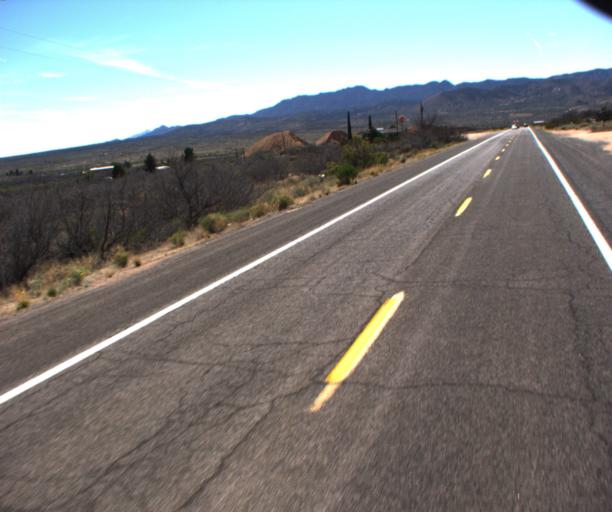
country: US
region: Arizona
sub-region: Mohave County
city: Peach Springs
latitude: 35.3647
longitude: -113.6808
